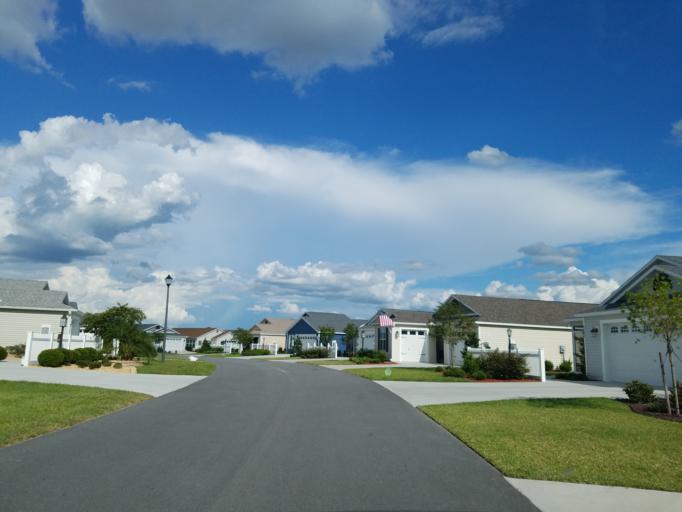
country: US
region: Florida
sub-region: Sumter County
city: Wildwood
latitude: 28.7957
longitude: -82.0330
